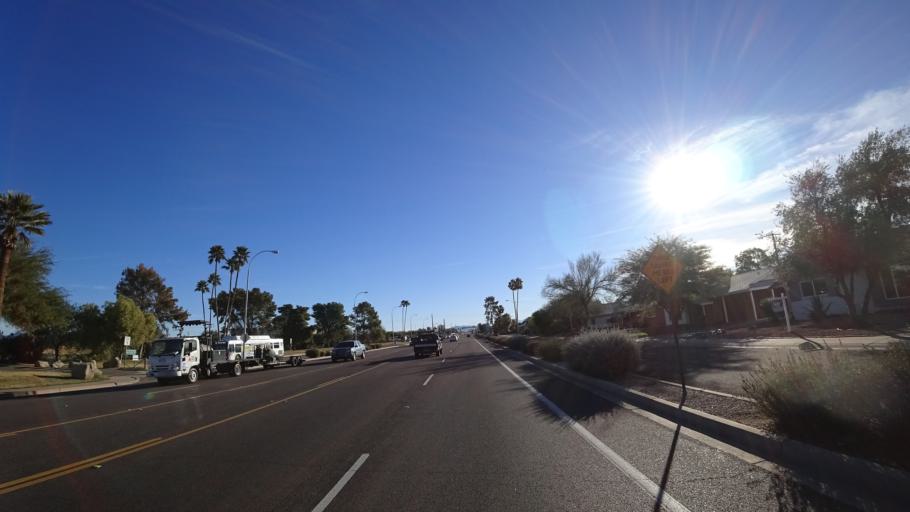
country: US
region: Arizona
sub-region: Maricopa County
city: Scottsdale
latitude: 33.4803
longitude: -111.8953
